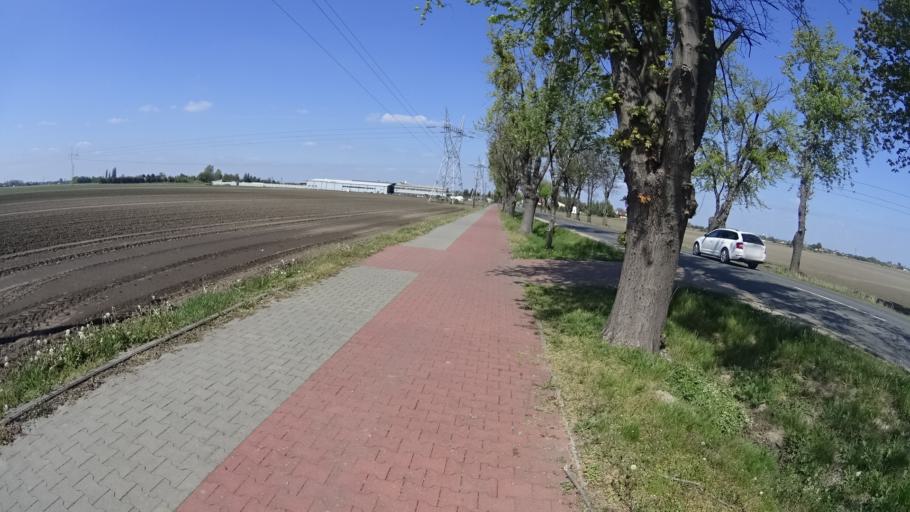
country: PL
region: Masovian Voivodeship
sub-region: Powiat warszawski zachodni
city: Stare Babice
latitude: 52.2367
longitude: 20.8167
